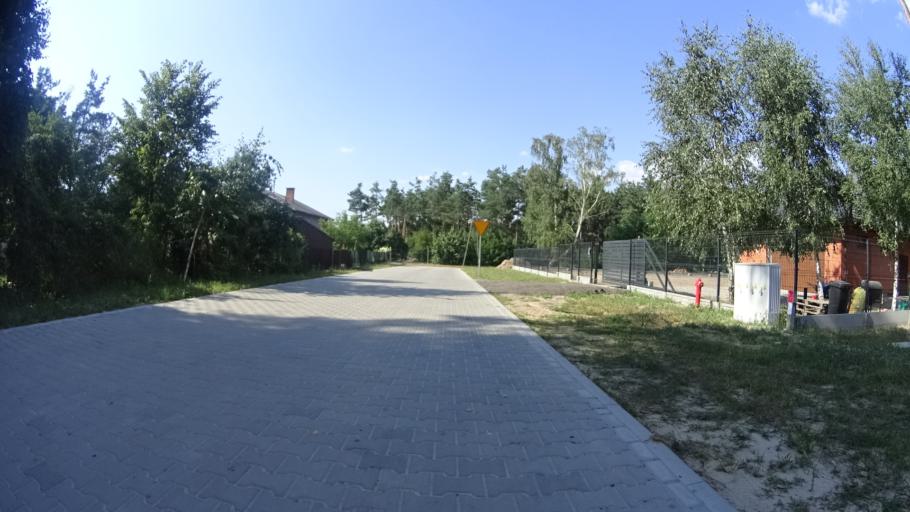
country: PL
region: Masovian Voivodeship
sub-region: Powiat bialobrzeski
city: Wysmierzyce
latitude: 51.6273
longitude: 20.8262
